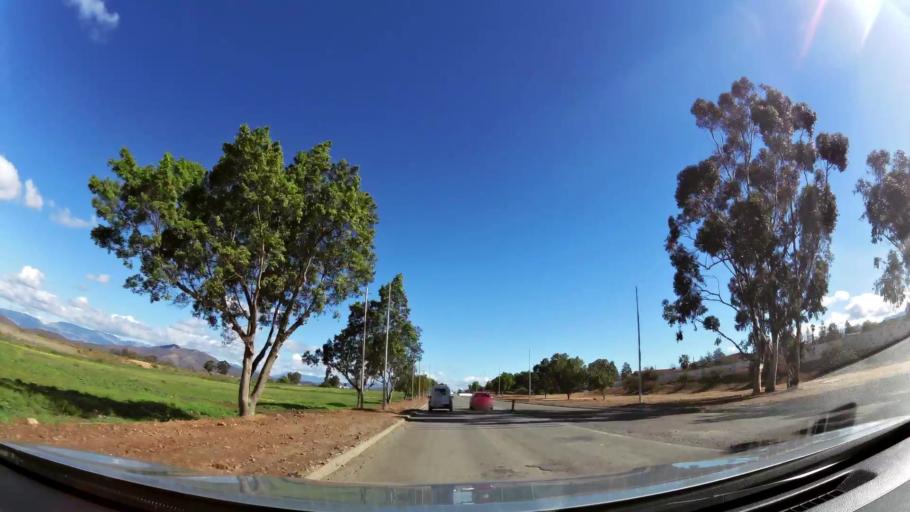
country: ZA
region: Western Cape
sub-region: Cape Winelands District Municipality
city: Ashton
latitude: -33.8356
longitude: 20.0475
